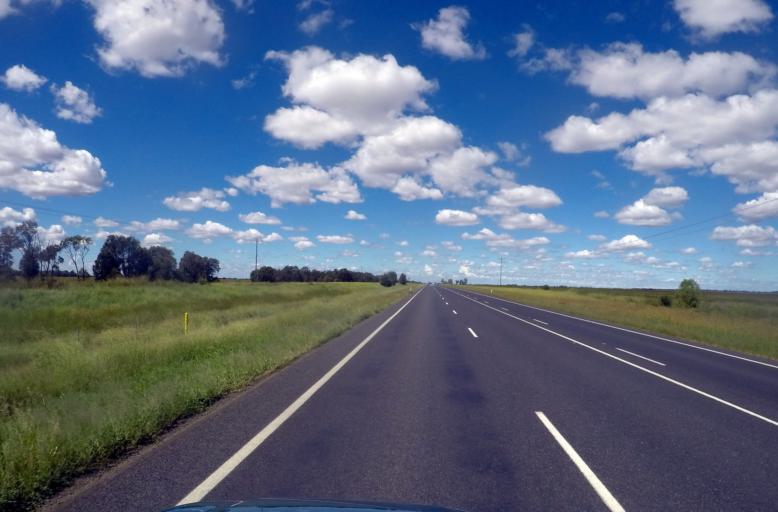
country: AU
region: Queensland
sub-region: Western Downs
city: Chinchilla
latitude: -26.8090
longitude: 150.7376
